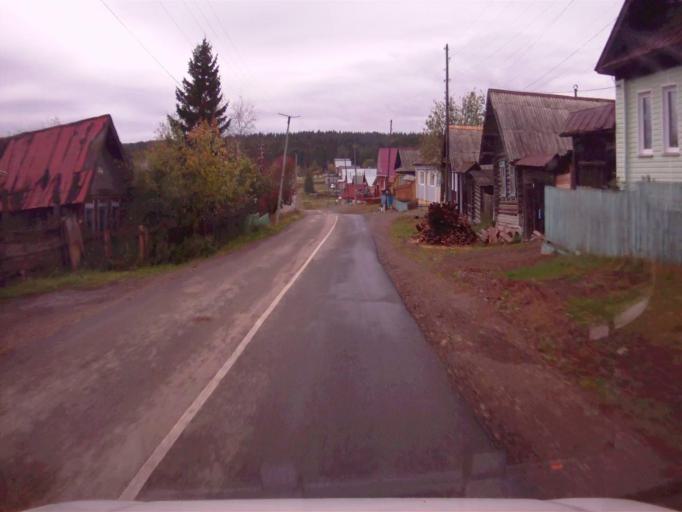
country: RU
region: Chelyabinsk
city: Nyazepetrovsk
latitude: 56.0625
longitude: 59.5744
